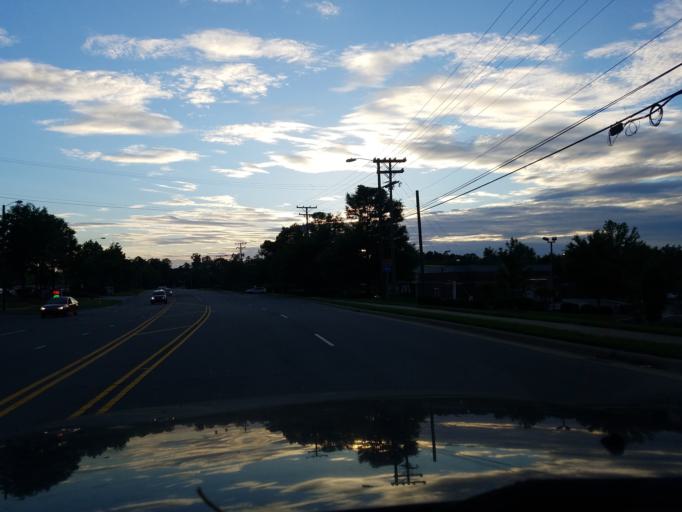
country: US
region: North Carolina
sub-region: Durham County
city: Durham
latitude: 35.9109
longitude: -78.9356
